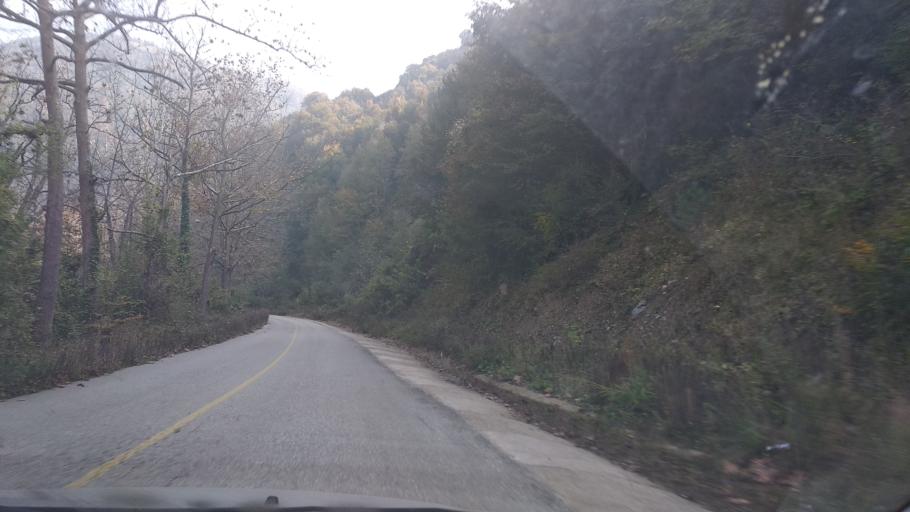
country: TR
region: Duzce
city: Kaynasli
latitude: 40.7272
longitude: 31.2554
